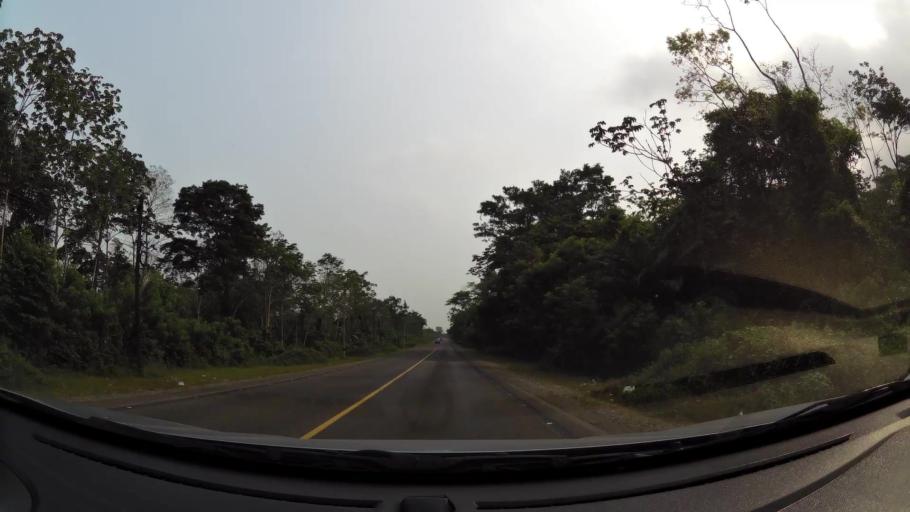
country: HN
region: Yoro
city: Toyos
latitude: 15.5645
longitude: -87.6192
